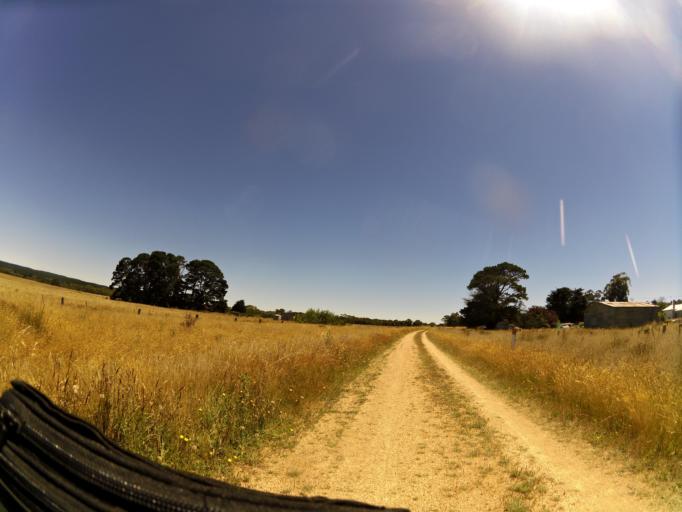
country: AU
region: Victoria
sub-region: Ballarat North
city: Delacombe
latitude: -37.6759
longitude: 143.6535
